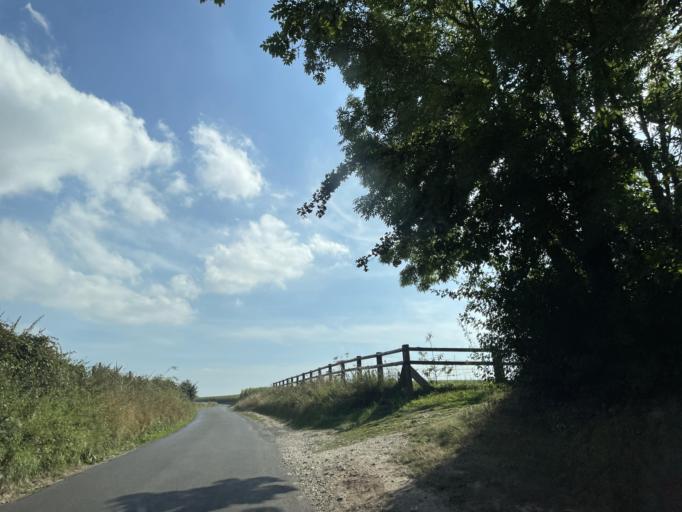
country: FR
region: Haute-Normandie
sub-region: Departement de la Seine-Maritime
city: Criel-sur-Mer
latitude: 50.0369
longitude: 1.3418
